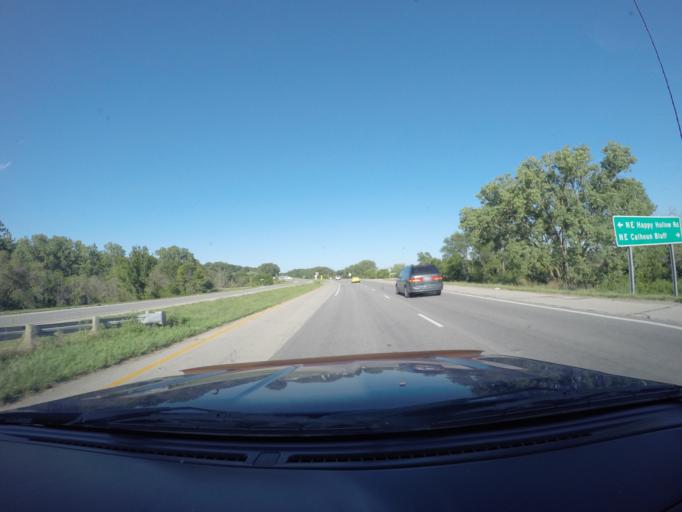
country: US
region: Kansas
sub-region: Shawnee County
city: Topeka
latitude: 39.0911
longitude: -95.6274
